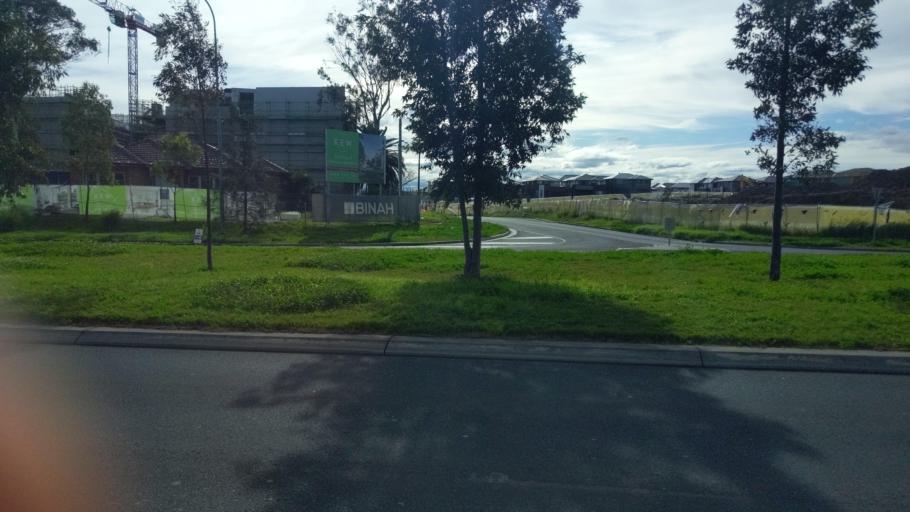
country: AU
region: New South Wales
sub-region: Blacktown
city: Riverstone
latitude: -33.6978
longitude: 150.8838
